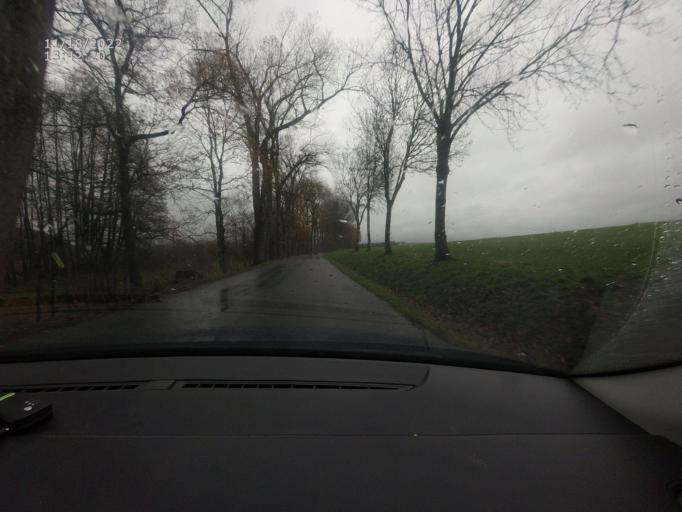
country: CZ
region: Plzensky
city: Kasejovice
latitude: 49.4361
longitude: 13.7952
